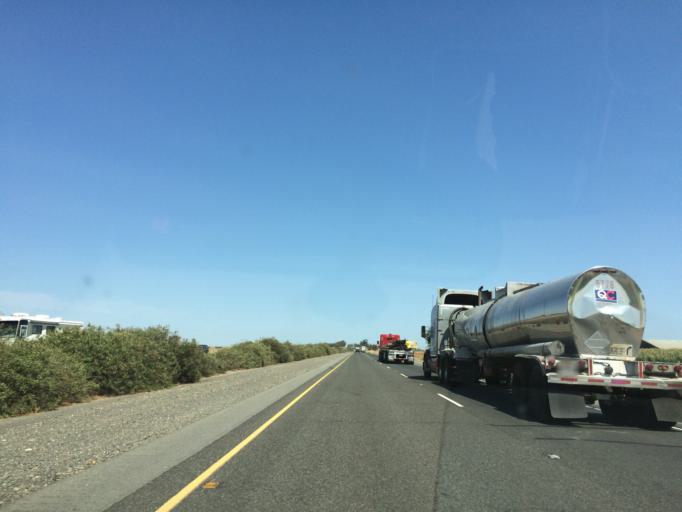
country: US
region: California
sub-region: Glenn County
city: Willows
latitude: 39.5700
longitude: -122.2122
